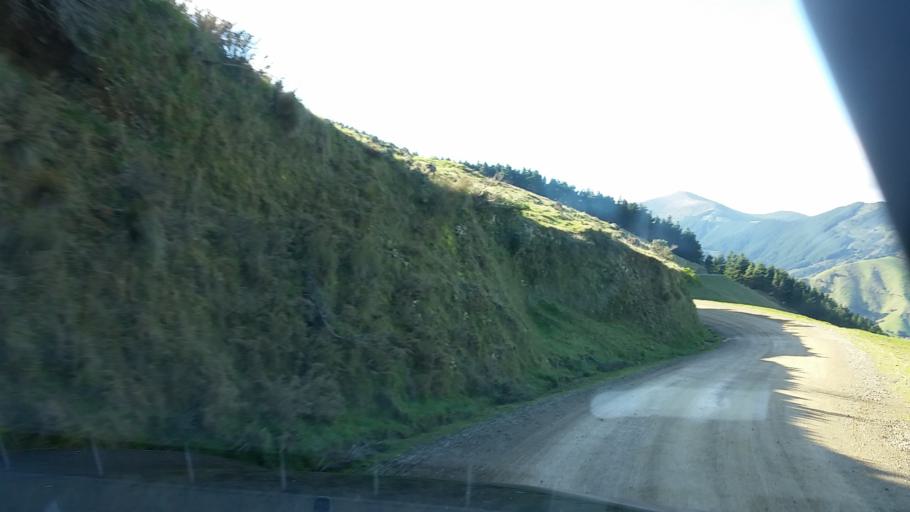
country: NZ
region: Marlborough
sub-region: Marlborough District
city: Picton
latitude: -40.9872
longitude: 173.8090
